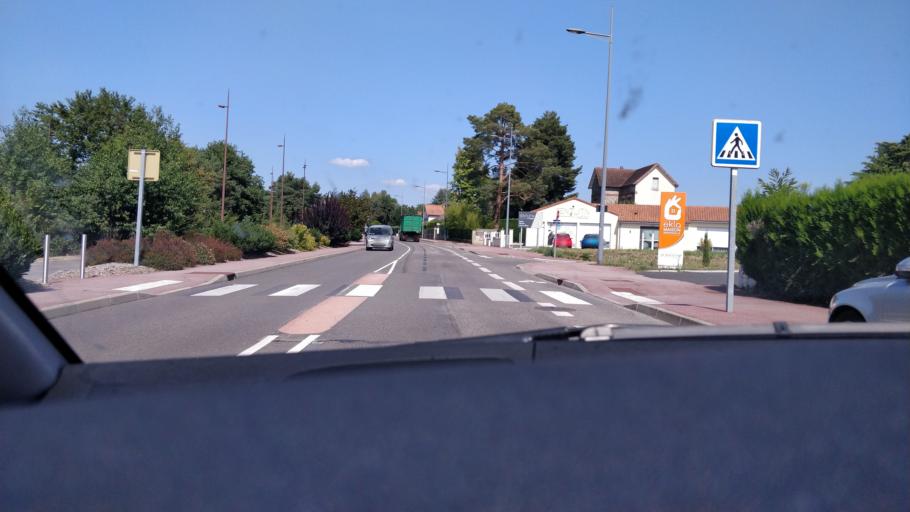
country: FR
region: Limousin
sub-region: Departement de la Haute-Vienne
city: Le Palais-sur-Vienne
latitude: 45.8575
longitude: 1.2854
